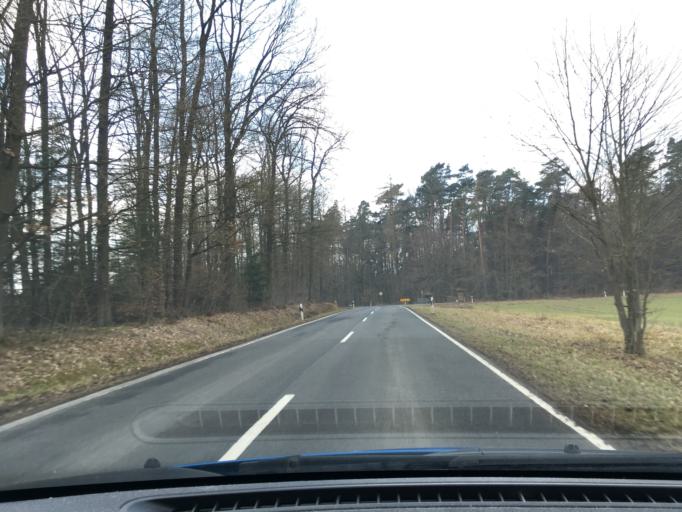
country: DE
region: Lower Saxony
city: Uslar
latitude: 51.5912
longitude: 9.6345
